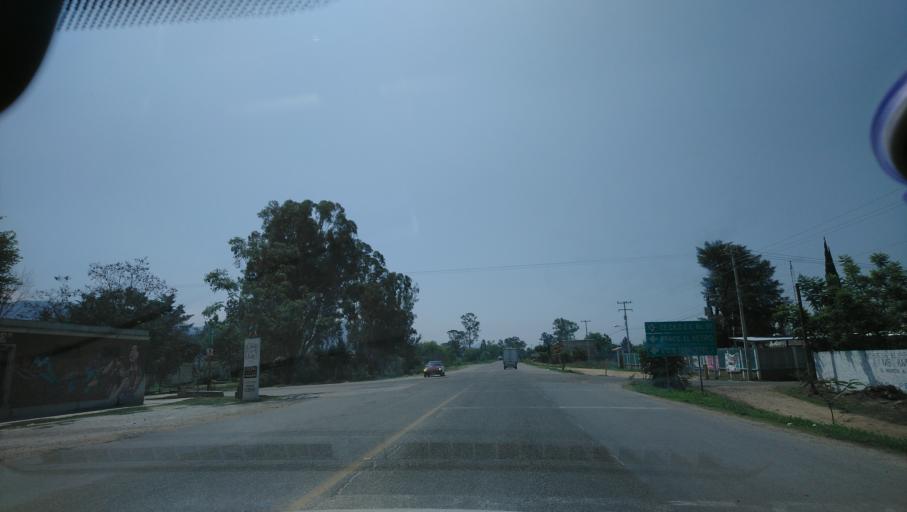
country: MX
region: Oaxaca
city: Santa Maria del Tule
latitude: 17.0439
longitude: -96.6312
